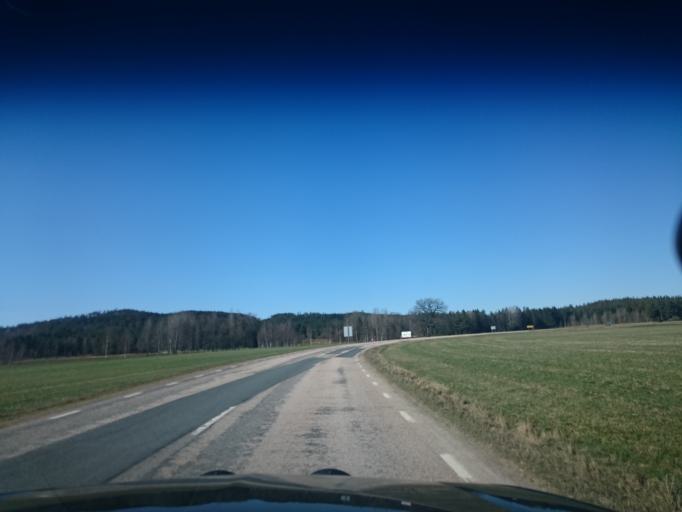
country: SE
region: Joenkoeping
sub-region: Vetlanda Kommun
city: Landsbro
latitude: 57.2071
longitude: 14.9448
